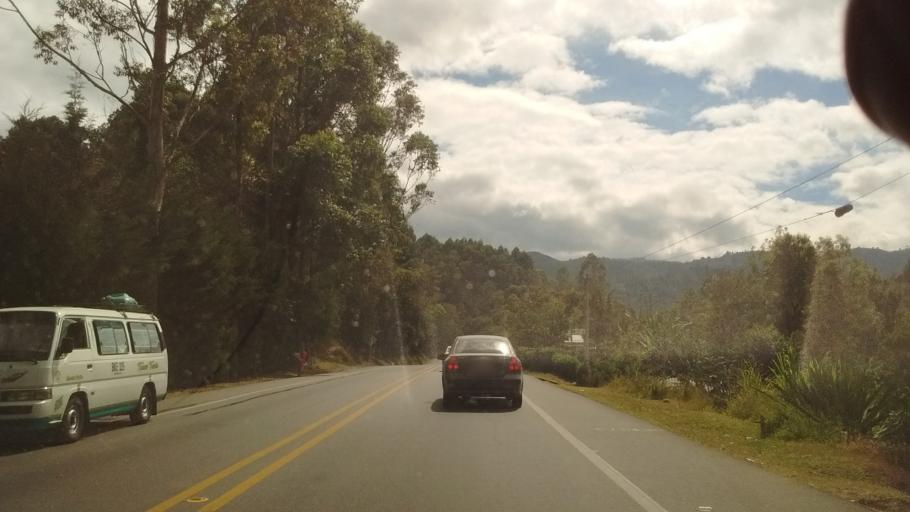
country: CO
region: Cauca
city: Cajibio
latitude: 2.6125
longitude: -76.5182
